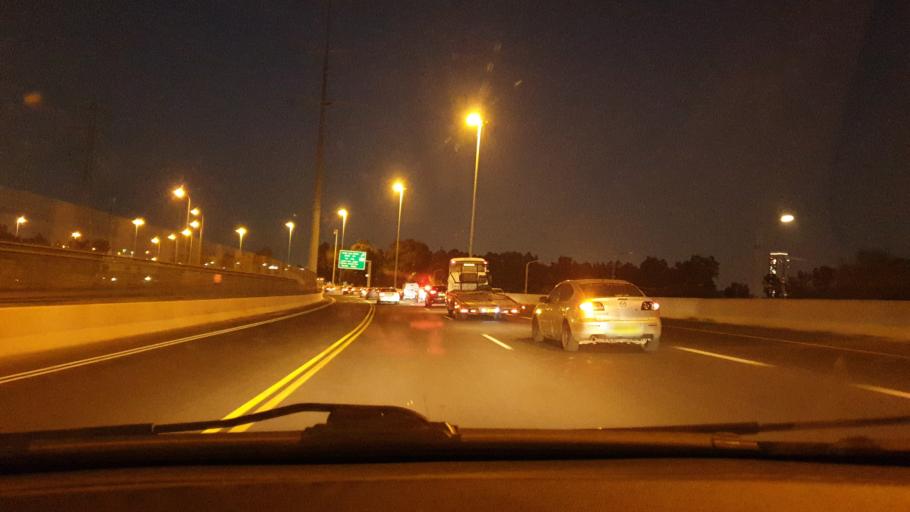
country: IL
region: Tel Aviv
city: Bat Yam
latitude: 32.0360
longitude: 34.7708
